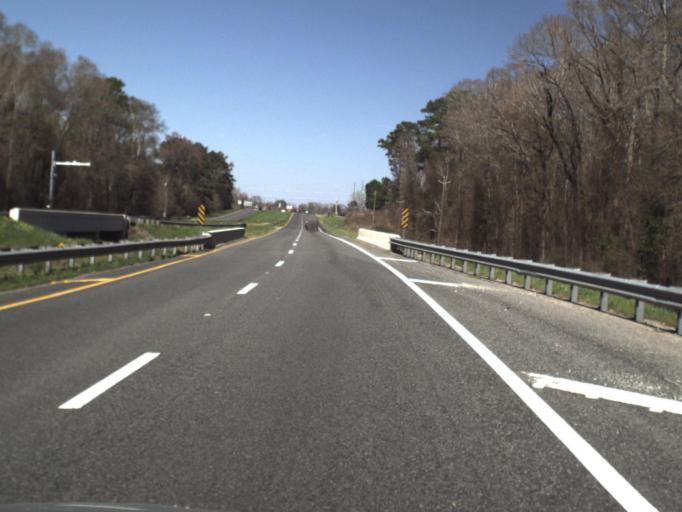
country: US
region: Florida
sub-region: Jackson County
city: Graceville
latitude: 30.9848
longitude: -85.4071
